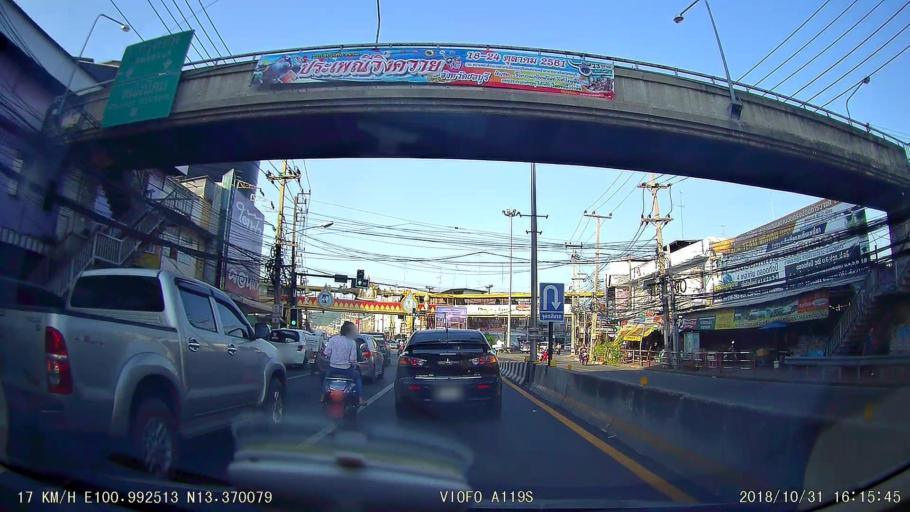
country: TH
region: Chon Buri
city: Chon Buri
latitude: 13.3702
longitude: 100.9925
